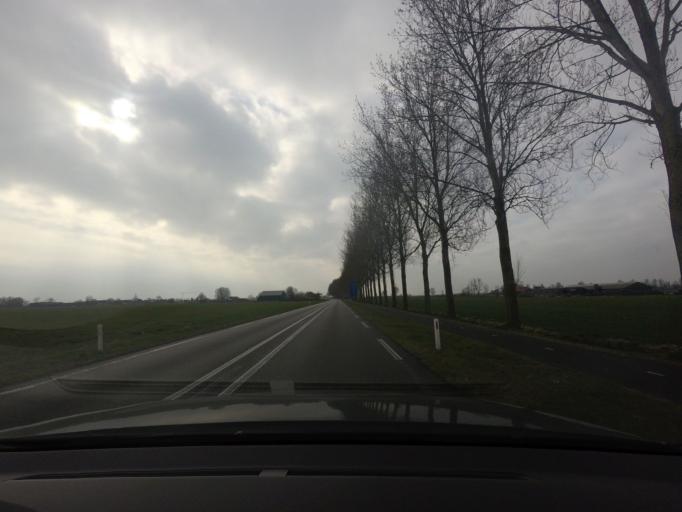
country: NL
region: Utrecht
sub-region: Gemeente De Ronde Venen
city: Mijdrecht
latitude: 52.1664
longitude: 4.9061
